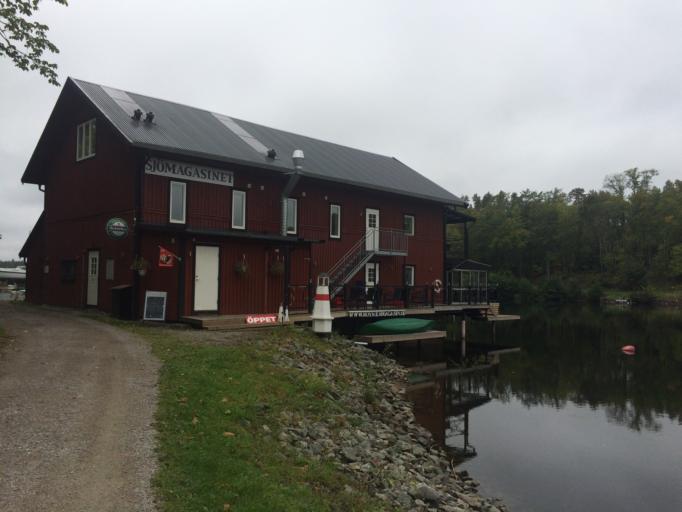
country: SE
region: Vaermland
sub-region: Arjangs Kommun
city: Arjaeng
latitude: 59.1934
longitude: 12.1069
